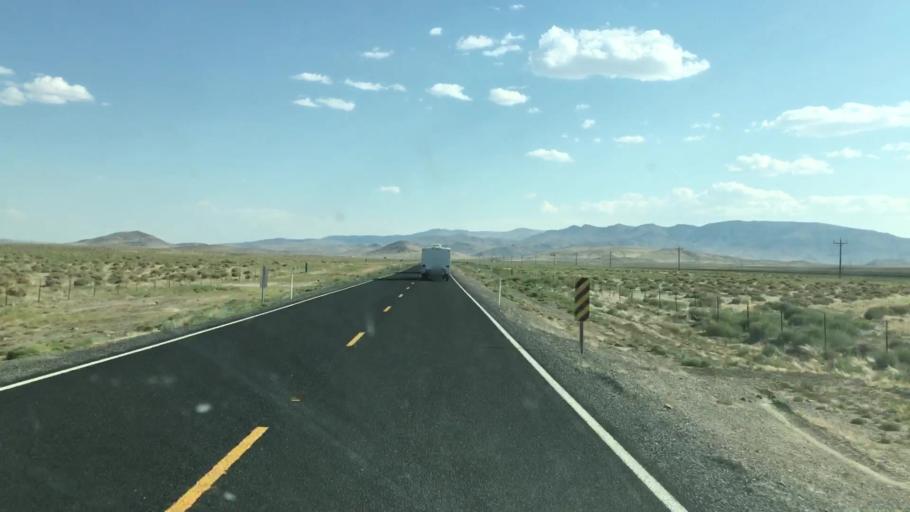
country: US
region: Nevada
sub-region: Lyon County
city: Fernley
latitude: 39.6693
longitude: -119.3319
